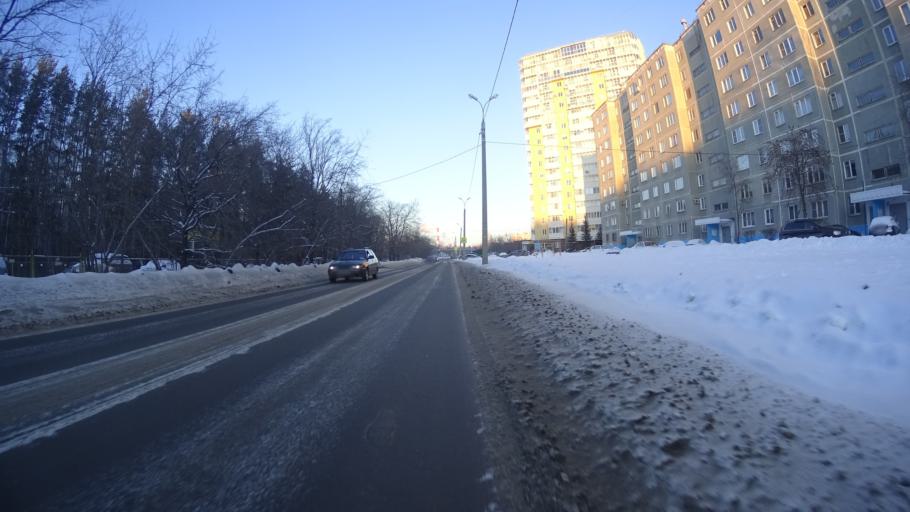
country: RU
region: Chelyabinsk
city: Roshchino
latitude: 55.1970
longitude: 61.2991
